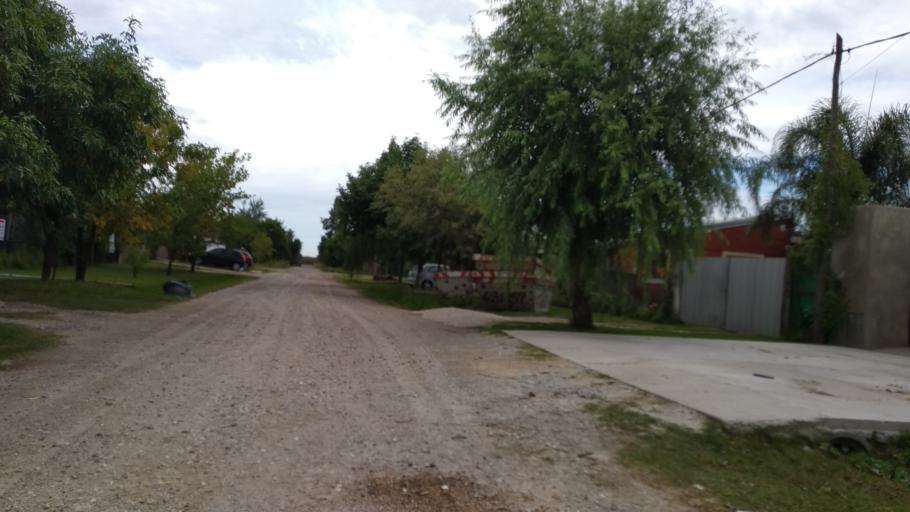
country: AR
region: Santa Fe
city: Funes
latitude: -32.9323
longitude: -60.8024
